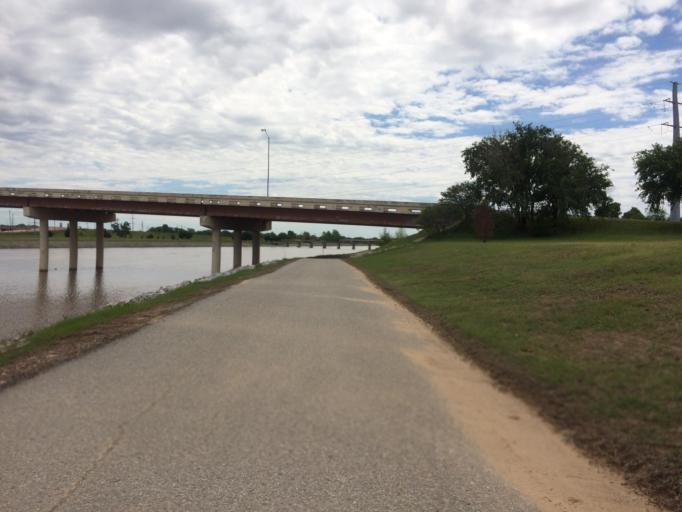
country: US
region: Oklahoma
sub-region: Oklahoma County
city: Oklahoma City
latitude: 35.4581
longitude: -97.5392
